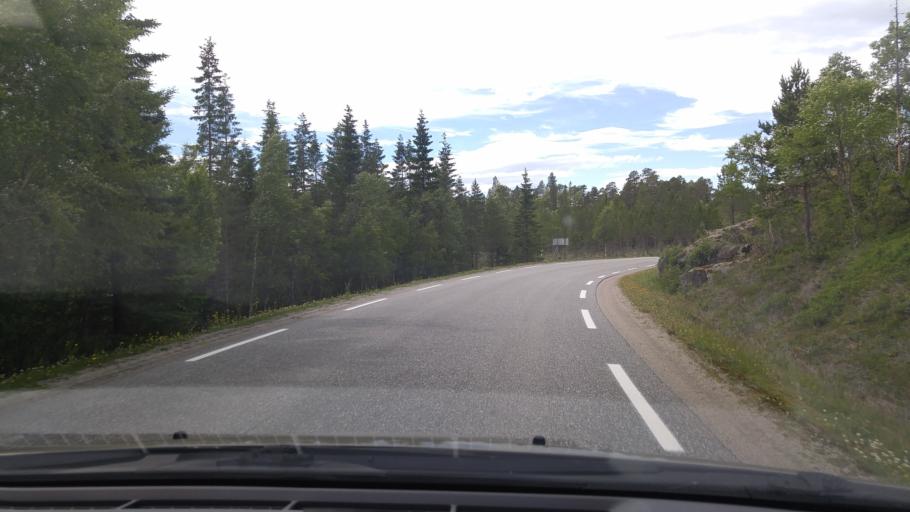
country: NO
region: Nord-Trondelag
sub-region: Namsos
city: Namsos
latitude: 64.6155
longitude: 11.4532
